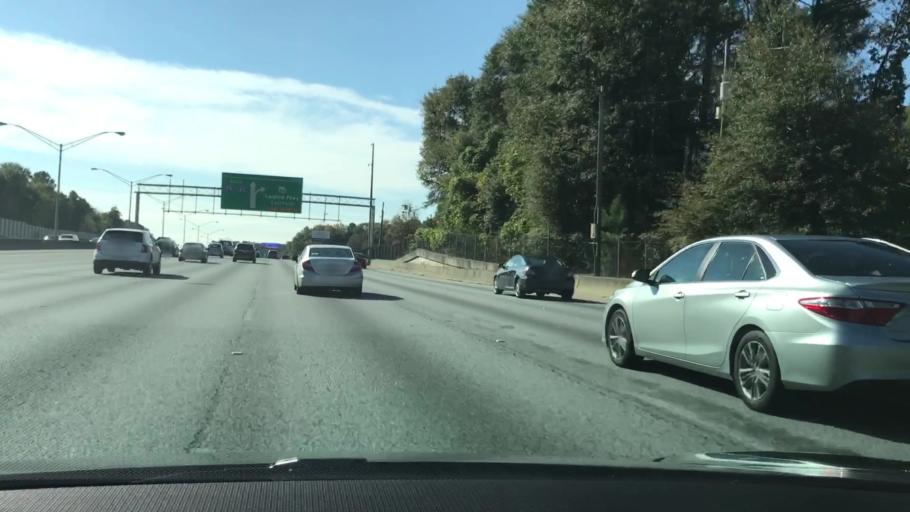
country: US
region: Georgia
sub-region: Fulton County
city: Atlanta
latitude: 33.7096
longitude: -84.4009
